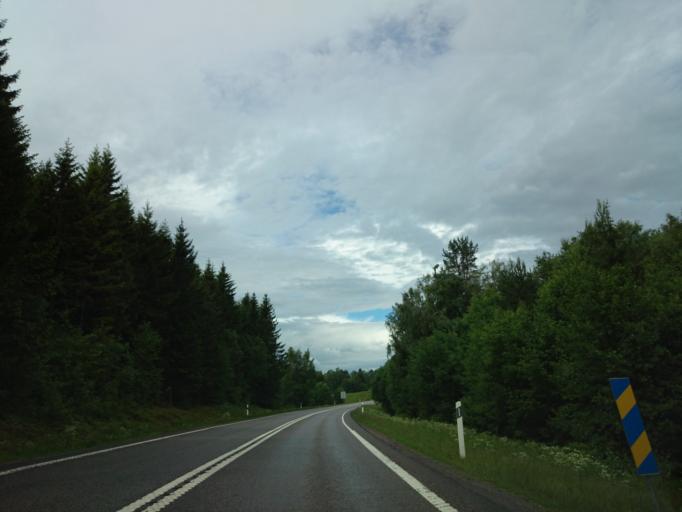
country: SE
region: OEstergoetland
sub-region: Motala Kommun
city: Motala
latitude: 58.6322
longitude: 14.9651
